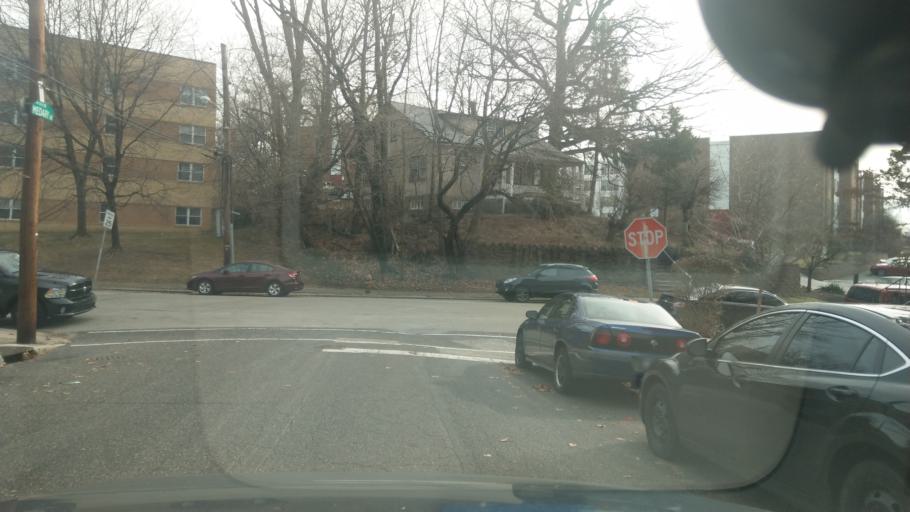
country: US
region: Pennsylvania
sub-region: Montgomery County
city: Wyncote
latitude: 40.0478
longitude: -75.1364
